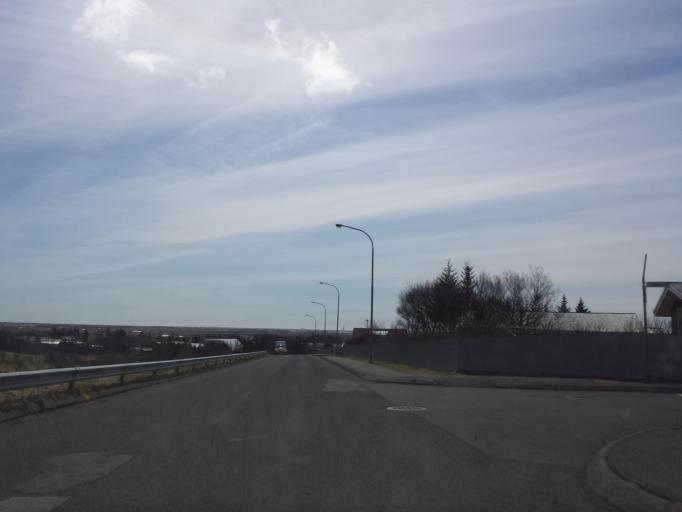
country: IS
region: South
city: Hveragerdi
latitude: 64.0041
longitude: -21.1848
